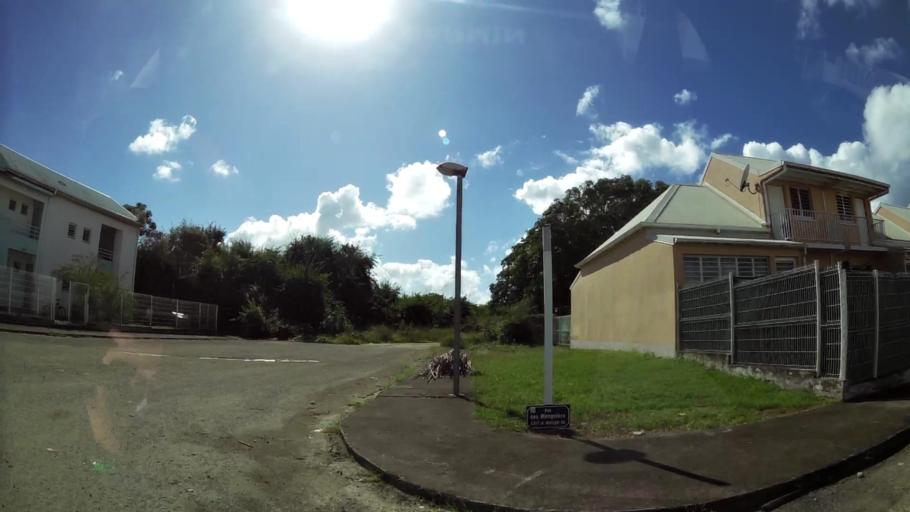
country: GP
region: Guadeloupe
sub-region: Guadeloupe
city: Port-Louis
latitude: 16.4125
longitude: -61.5278
